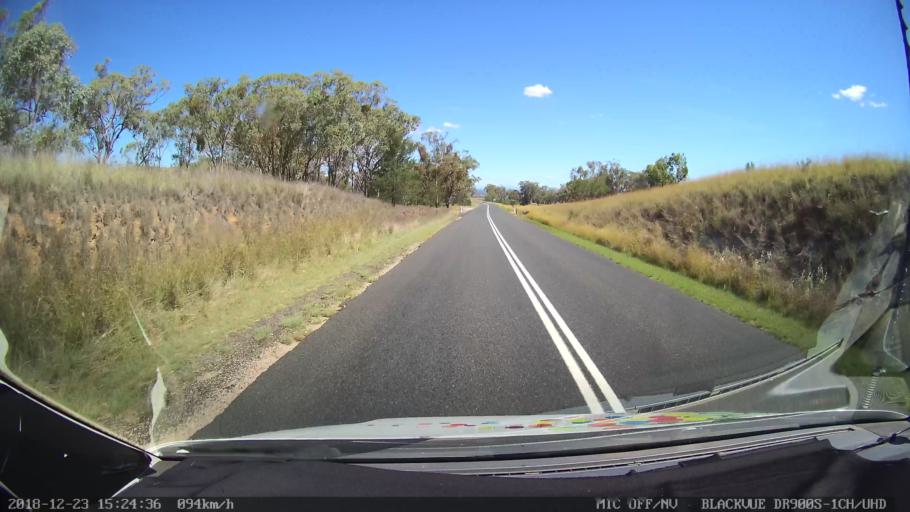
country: AU
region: New South Wales
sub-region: Tamworth Municipality
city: Manilla
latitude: -30.8939
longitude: 150.8243
